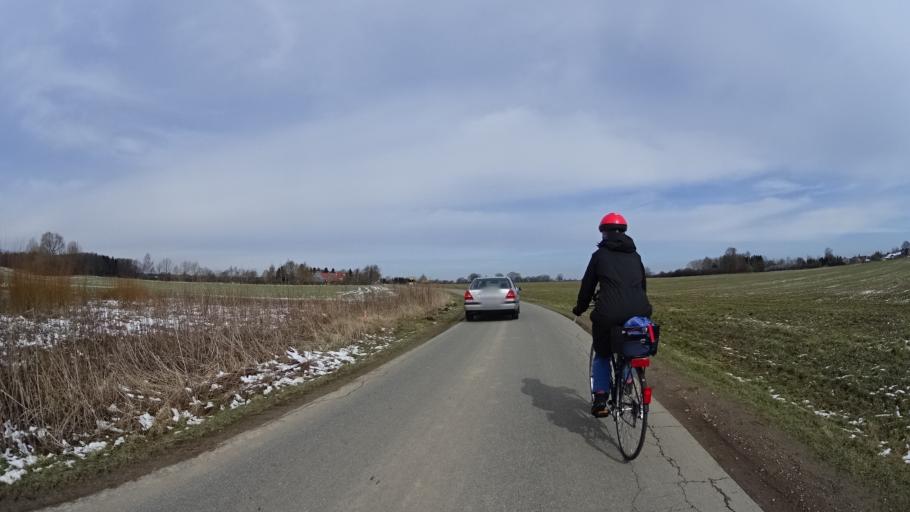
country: DE
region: Schleswig-Holstein
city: Rendswuhren
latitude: 54.0862
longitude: 10.1999
